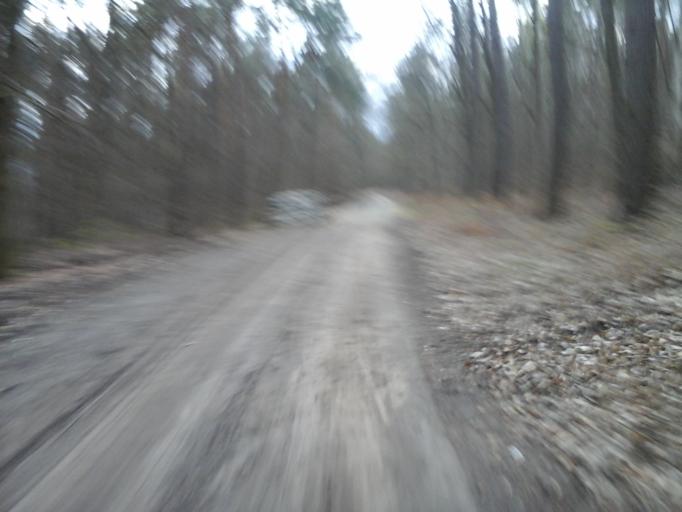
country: PL
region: West Pomeranian Voivodeship
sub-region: Powiat choszczenski
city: Bierzwnik
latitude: 53.0289
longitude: 15.6547
